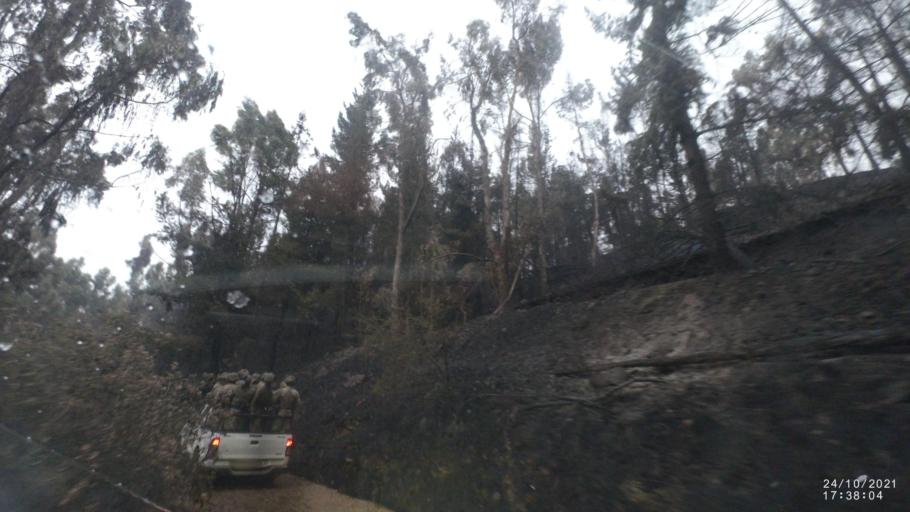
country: BO
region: Cochabamba
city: Cochabamba
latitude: -17.3177
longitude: -66.1297
